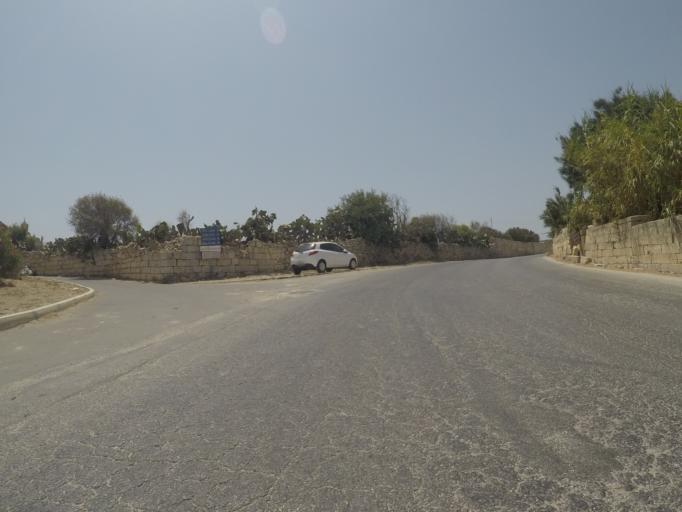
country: MT
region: Is-Siggiewi
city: Siggiewi
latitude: 35.8431
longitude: 14.4344
